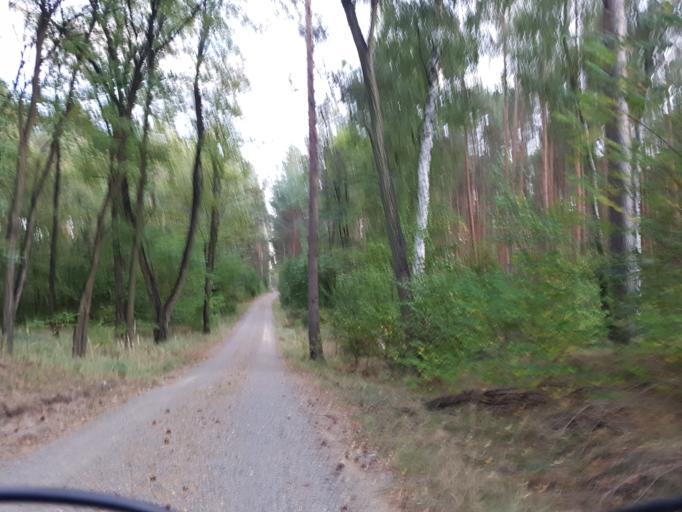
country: DE
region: Brandenburg
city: Trobitz
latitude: 51.5747
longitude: 13.4602
